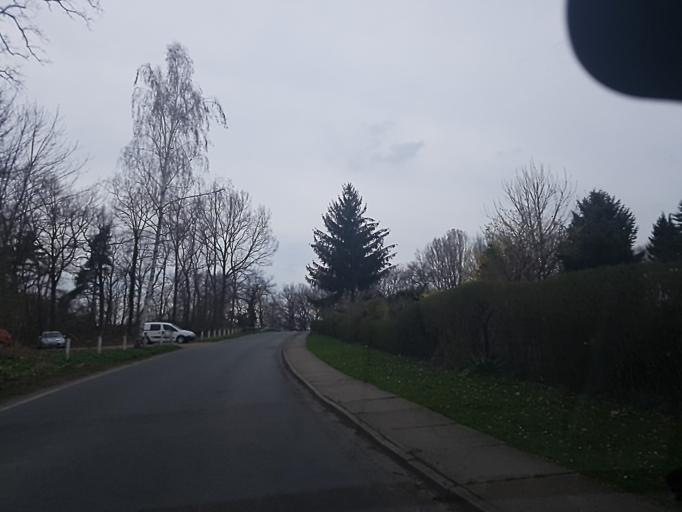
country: DE
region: Saxony
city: Oschatz
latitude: 51.2916
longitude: 13.0937
